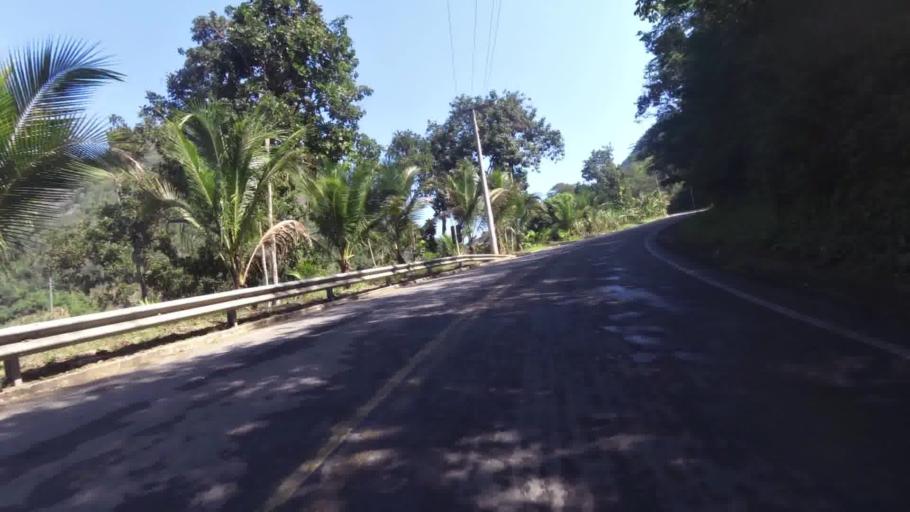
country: BR
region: Espirito Santo
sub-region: Alfredo Chaves
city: Alfredo Chaves
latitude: -20.6157
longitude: -40.7813
